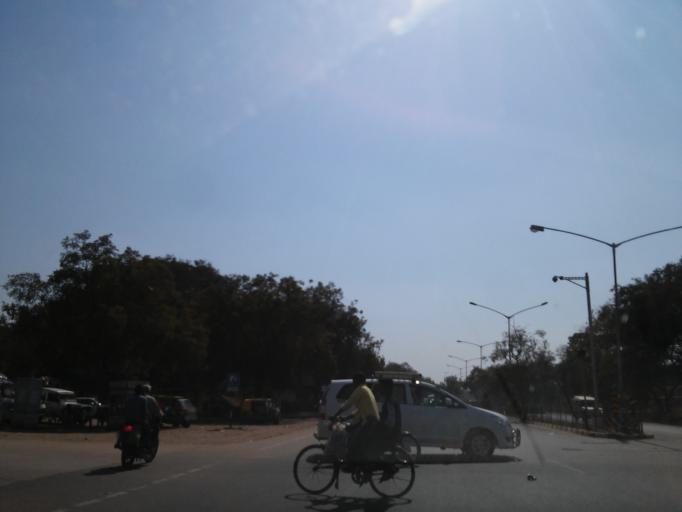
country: IN
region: Gujarat
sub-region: Gandhinagar
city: Ghandinagar
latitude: 23.2339
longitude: 72.6760
